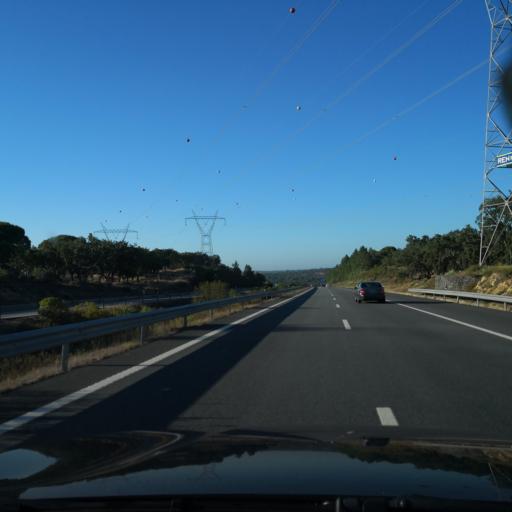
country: PT
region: Setubal
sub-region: Alcacer do Sal
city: Alcacer do Sal
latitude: 38.4452
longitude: -8.5250
